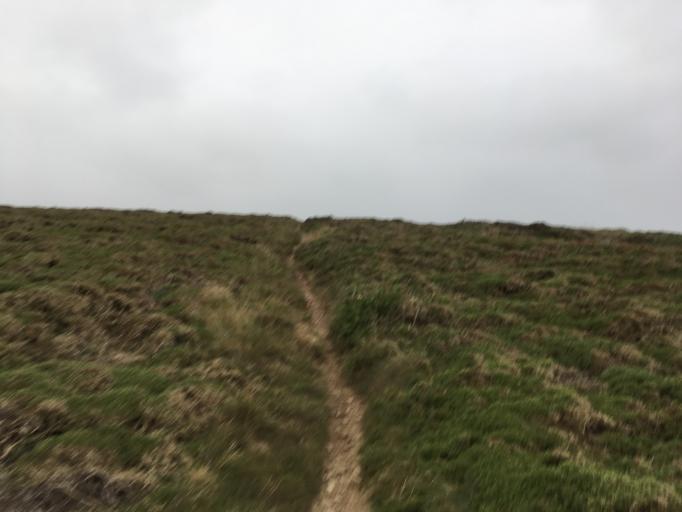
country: FR
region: Brittany
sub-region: Departement du Finistere
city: Plogoff
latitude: 48.0519
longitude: -4.7084
